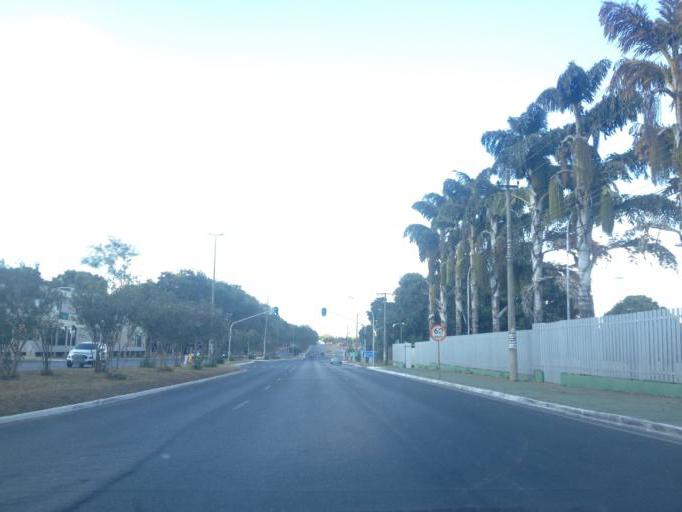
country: BR
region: Federal District
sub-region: Brasilia
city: Brasilia
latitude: -15.8366
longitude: -47.9168
